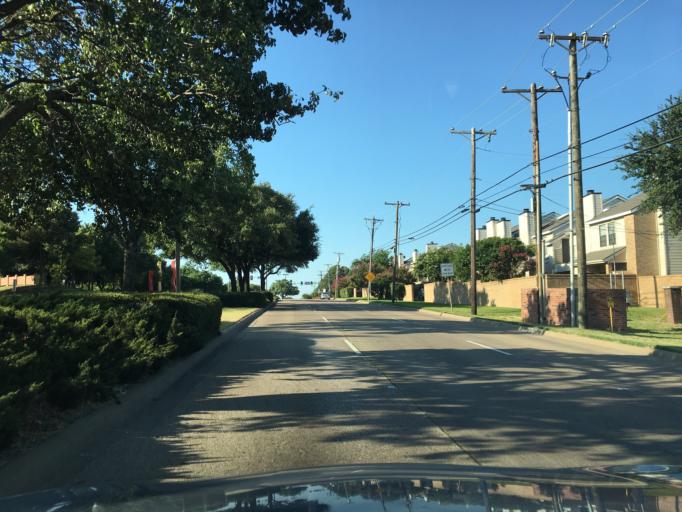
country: US
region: Texas
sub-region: Dallas County
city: Addison
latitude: 32.9520
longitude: -96.8558
